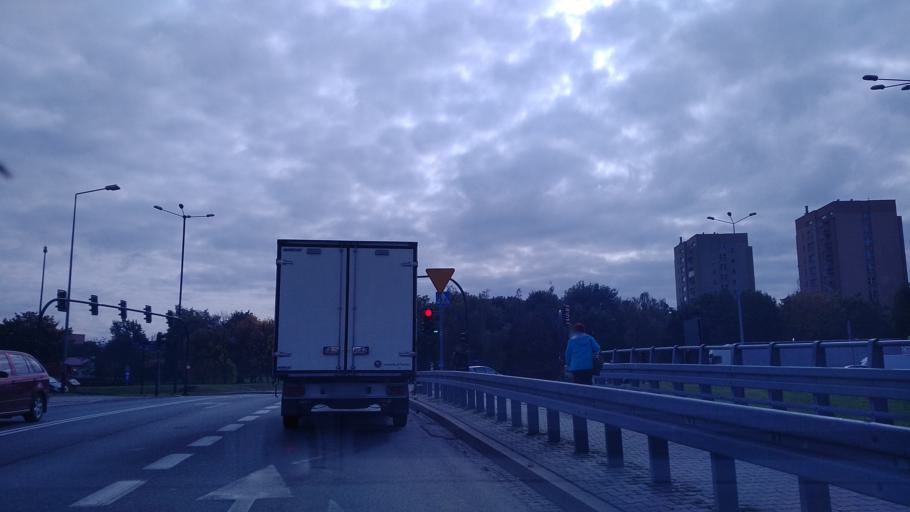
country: PL
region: Lesser Poland Voivodeship
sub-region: Powiat krakowski
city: Zielonki
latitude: 50.0910
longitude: 19.9186
